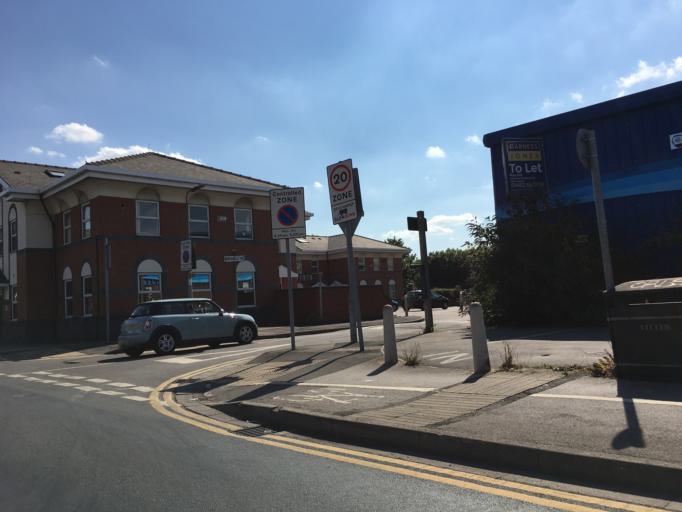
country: GB
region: England
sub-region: City of Kingston upon Hull
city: Hull
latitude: 53.7495
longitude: -0.3406
